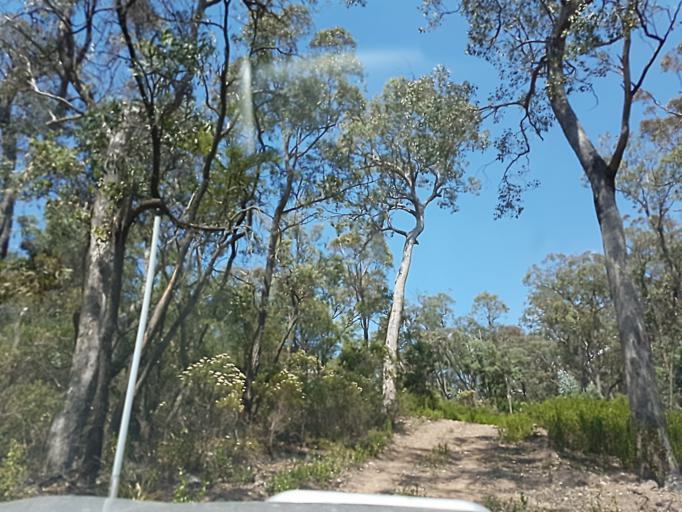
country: AU
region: Victoria
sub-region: East Gippsland
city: Lakes Entrance
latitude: -37.3094
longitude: 148.3594
